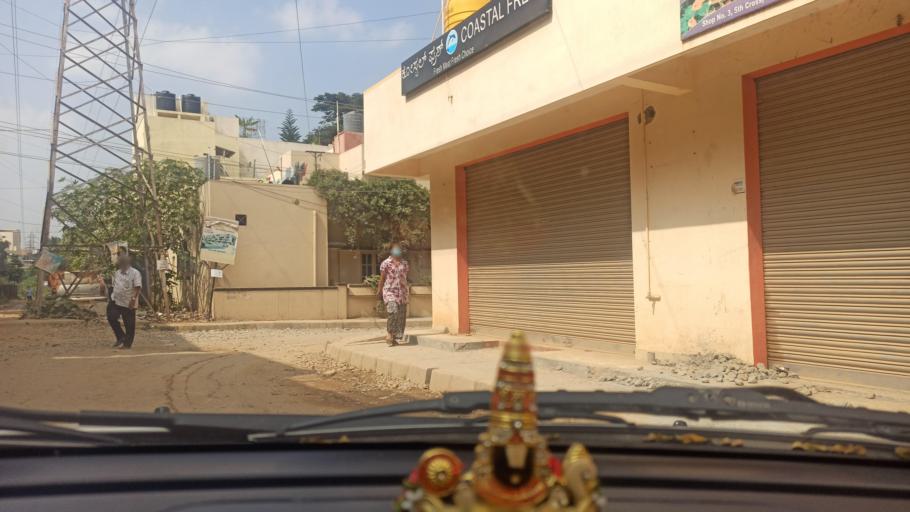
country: IN
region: Karnataka
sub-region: Bangalore Urban
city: Bangalore
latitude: 13.0168
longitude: 77.6654
